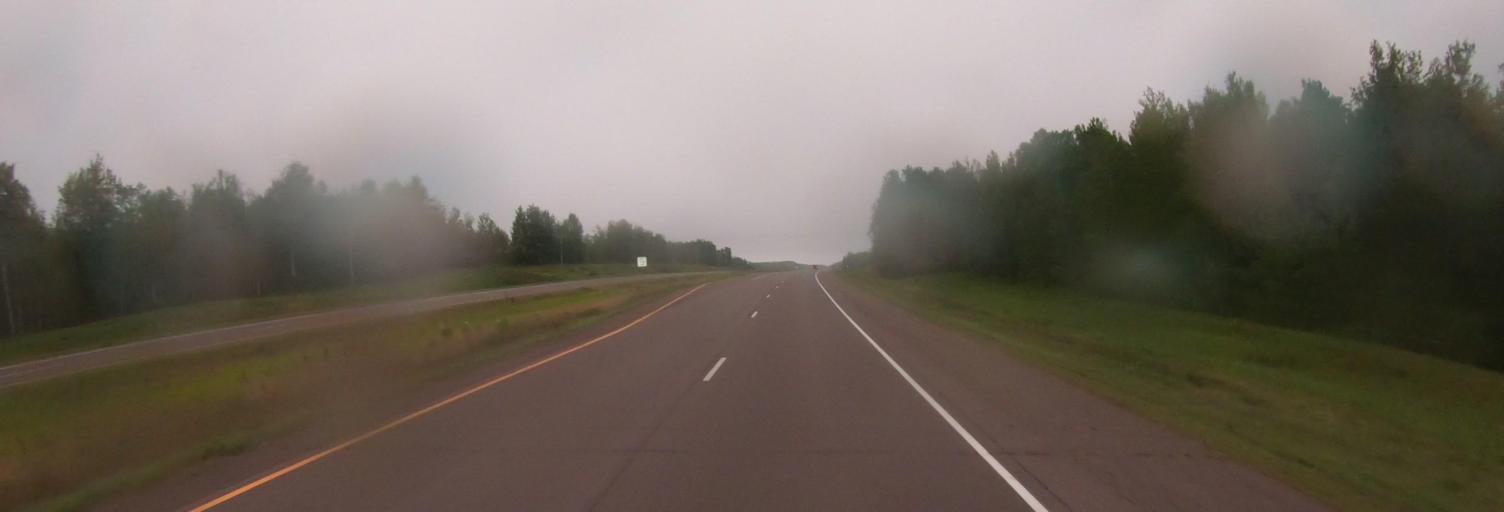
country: US
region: Minnesota
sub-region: Carlton County
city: Cloquet
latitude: 46.9153
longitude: -92.4702
